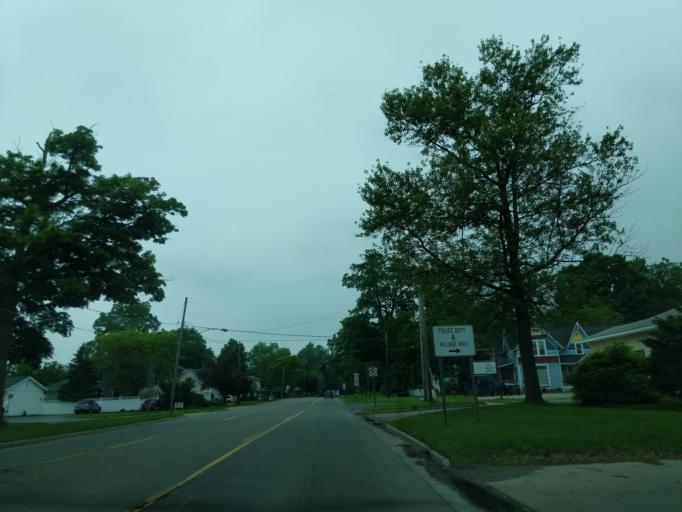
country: US
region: Michigan
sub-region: Branch County
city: Quincy
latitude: 41.9434
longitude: -84.8870
